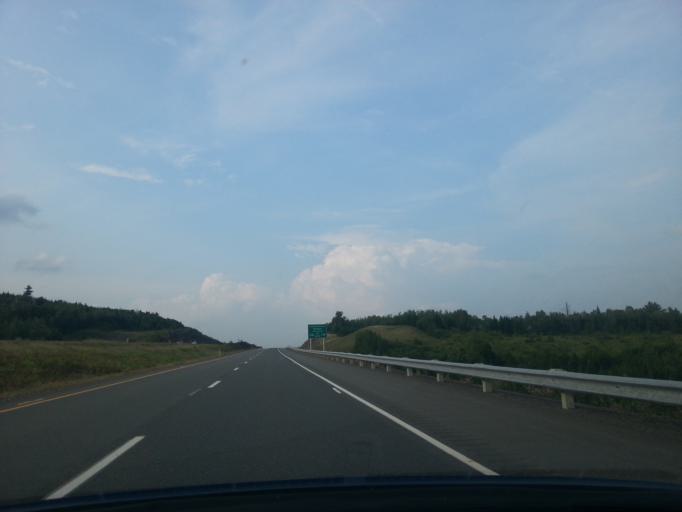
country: US
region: Maine
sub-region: Aroostook County
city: Fort Fairfield
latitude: 46.7096
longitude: -67.7362
